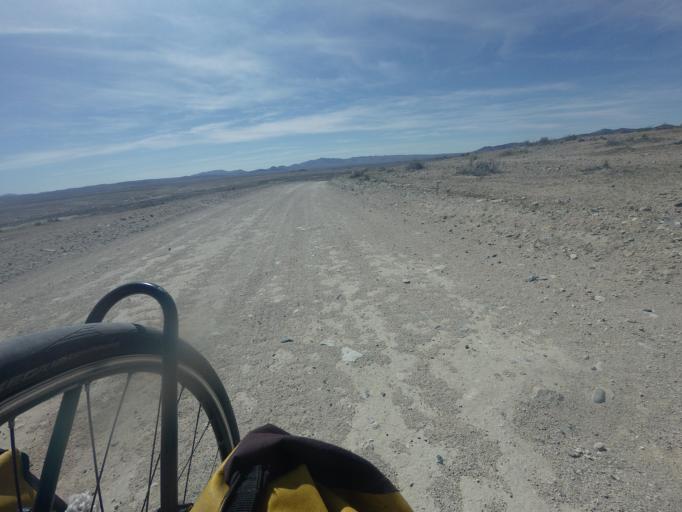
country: US
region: California
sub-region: San Bernardino County
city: Searles Valley
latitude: 35.6008
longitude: -117.3826
